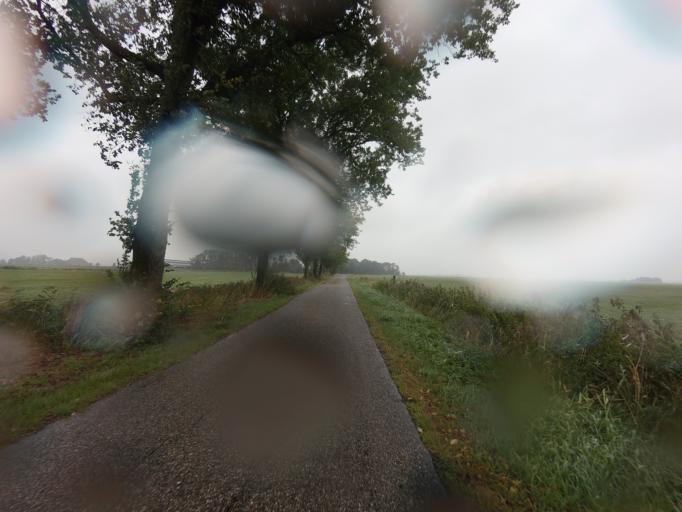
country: NL
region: Friesland
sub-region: Gemeente Boarnsterhim
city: Aldeboarn
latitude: 53.0718
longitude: 5.9288
